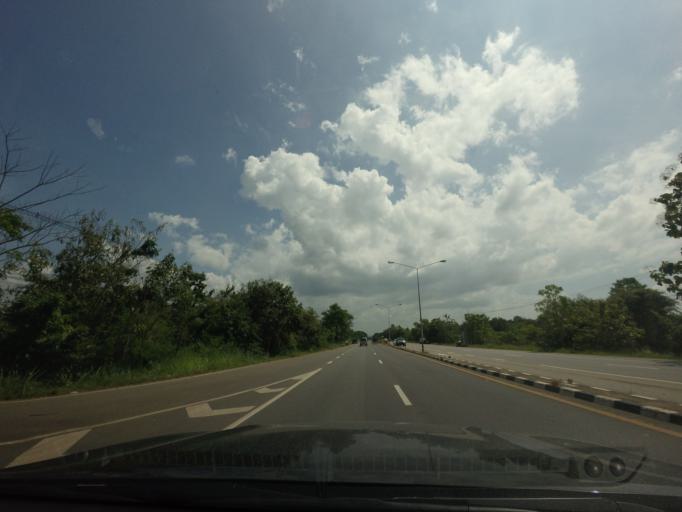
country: TH
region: Phetchabun
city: Phetchabun
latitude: 16.2357
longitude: 101.0809
